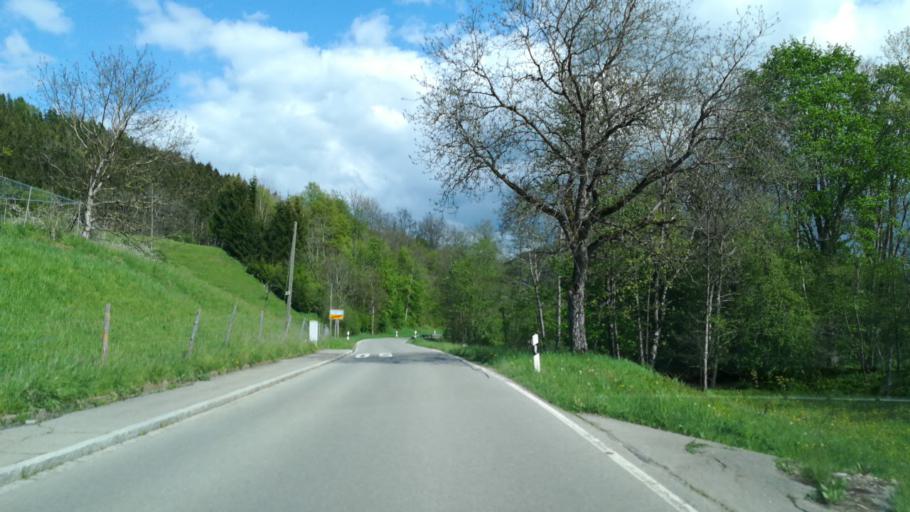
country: DE
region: Baden-Wuerttemberg
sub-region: Freiburg Region
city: Blumberg
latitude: 47.8397
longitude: 8.4915
